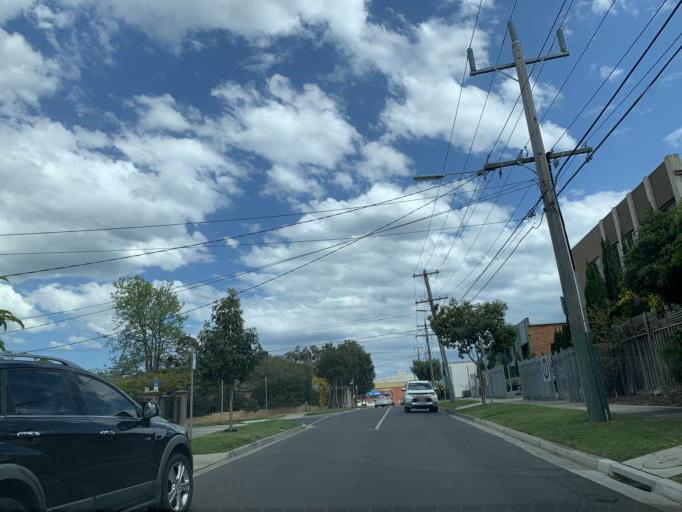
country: AU
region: Victoria
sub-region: Bayside
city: Highett
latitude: -37.9551
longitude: 145.0423
